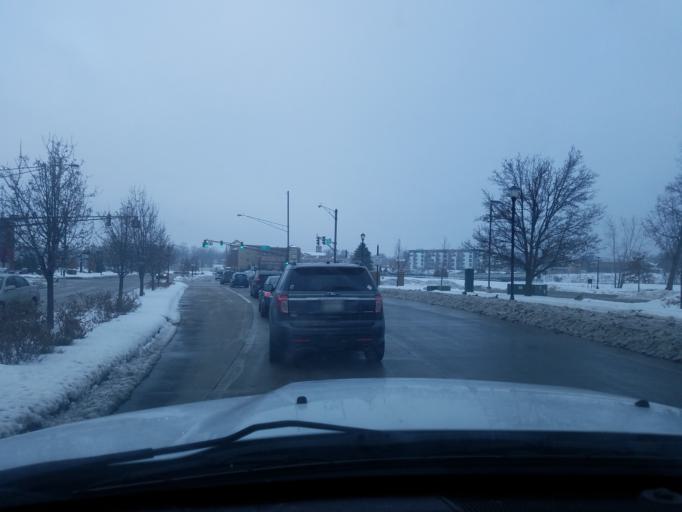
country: US
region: Indiana
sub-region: Saint Joseph County
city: Mishawaka
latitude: 41.6627
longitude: -86.1797
